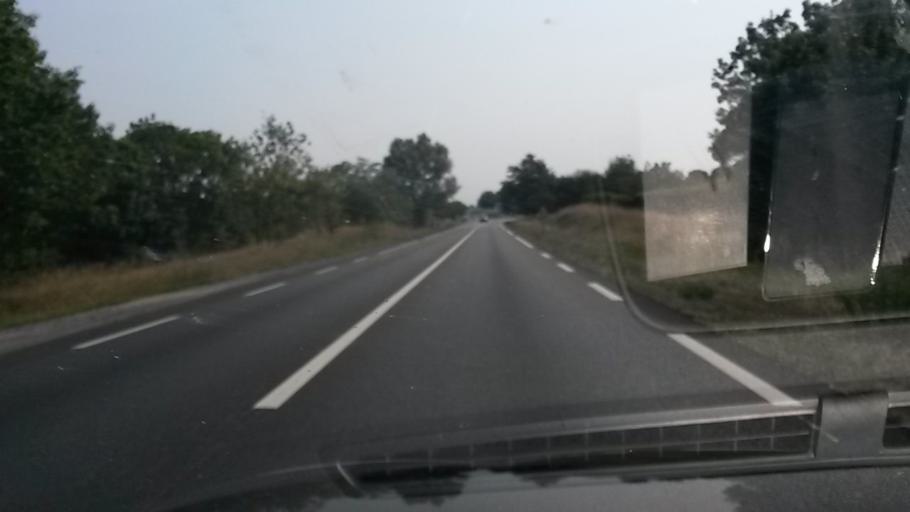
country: FR
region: Pays de la Loire
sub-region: Departement de la Loire-Atlantique
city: Ancenis
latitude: 47.3850
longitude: -1.1726
